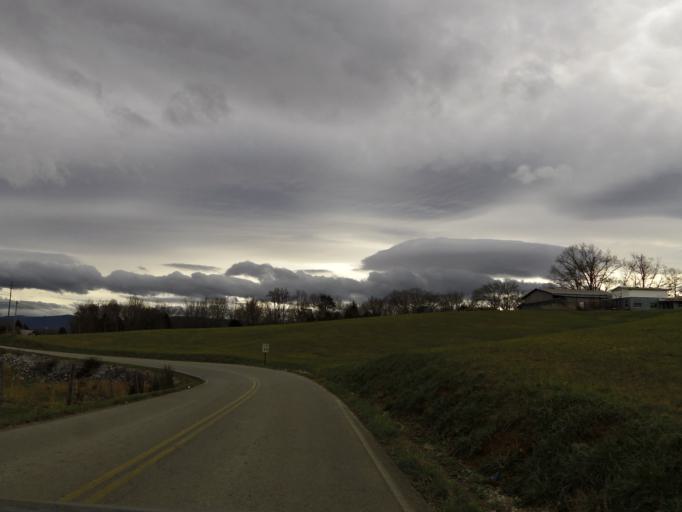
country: US
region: Tennessee
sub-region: Greene County
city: Tusculum
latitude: 36.2089
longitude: -82.7481
